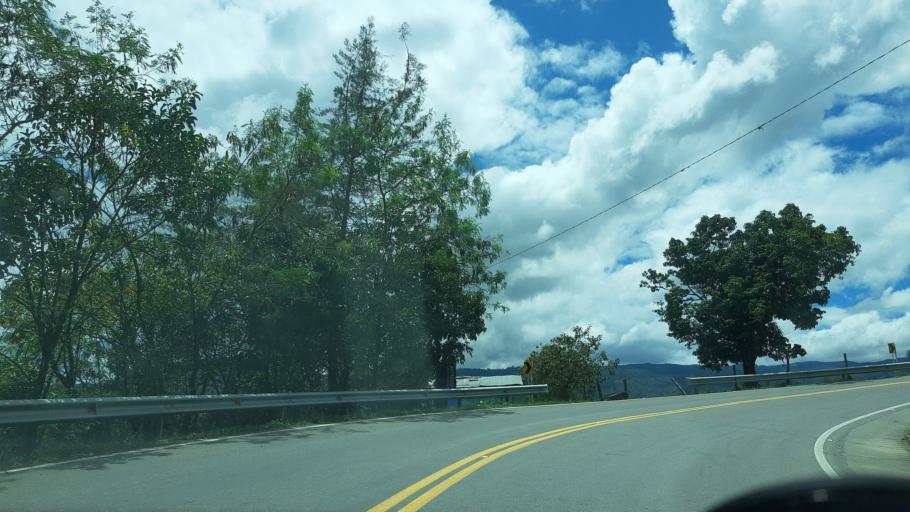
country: CO
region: Boyaca
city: Guateque
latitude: 5.0109
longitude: -73.4597
